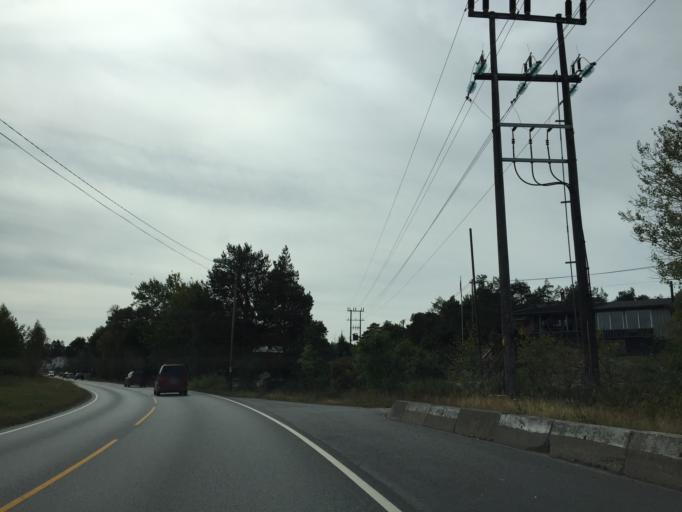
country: NO
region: Ostfold
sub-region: Fredrikstad
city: Fredrikstad
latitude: 59.1185
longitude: 10.9079
